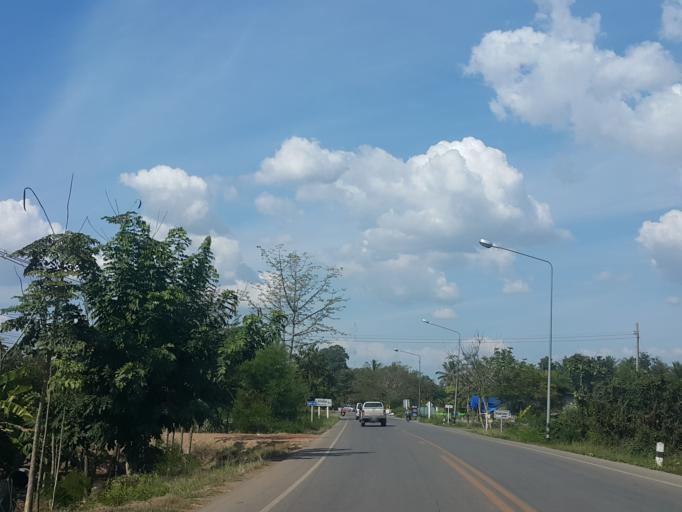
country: TH
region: Sukhothai
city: Sawankhalok
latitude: 17.2845
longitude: 99.8348
